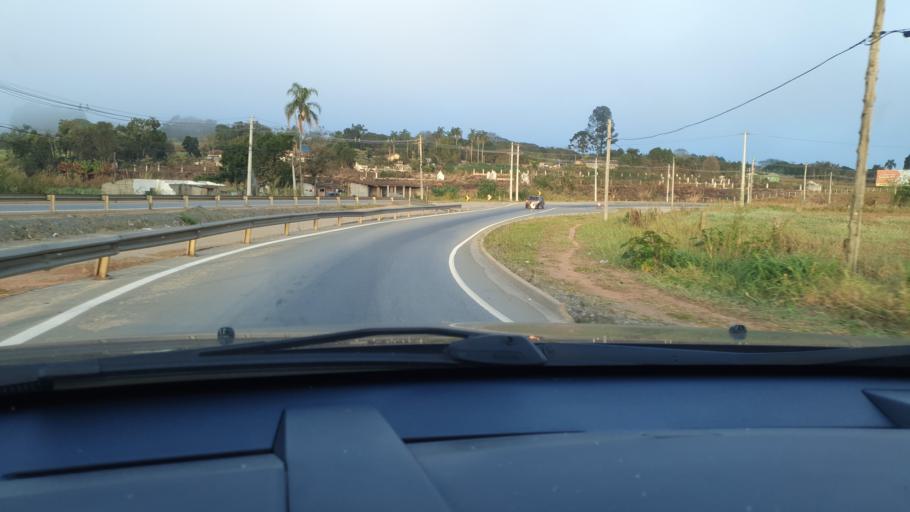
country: BR
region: Sao Paulo
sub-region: Ibiuna
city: Ibiuna
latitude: -23.6472
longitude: -47.1595
